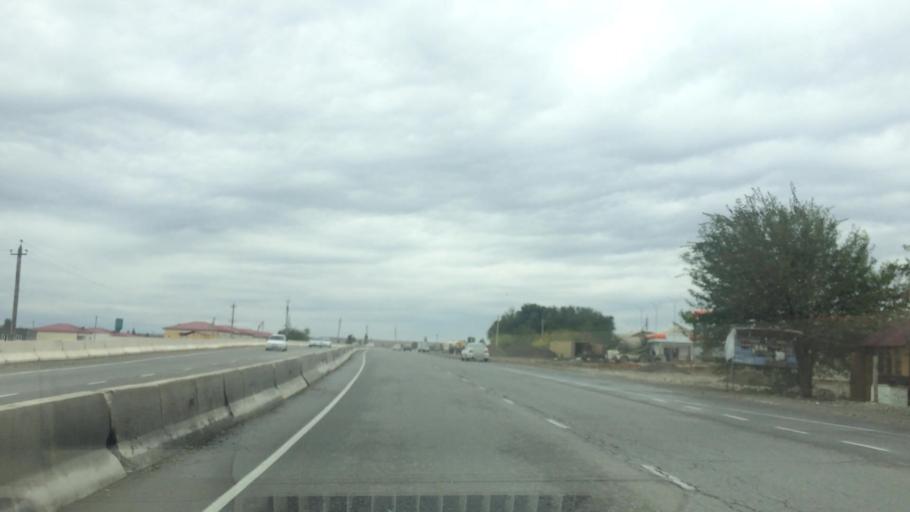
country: UZ
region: Jizzax
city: Jizzax
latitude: 39.9753
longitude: 67.5612
